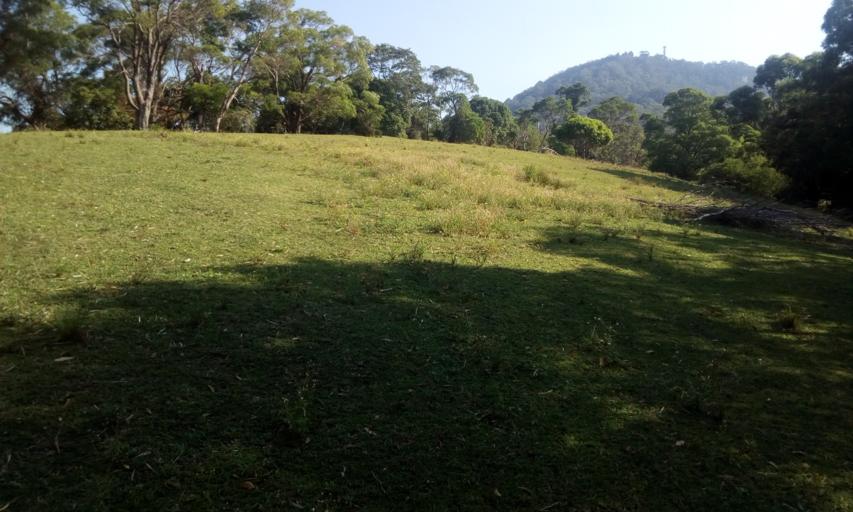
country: AU
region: New South Wales
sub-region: Wollongong
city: Mount Ousley
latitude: -34.4030
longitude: 150.8716
